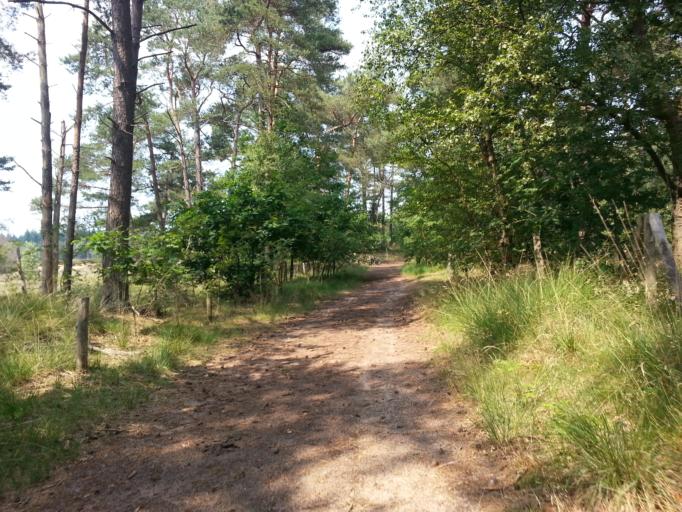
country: NL
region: Utrecht
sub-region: Gemeente Amersfoort
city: Randenbroek
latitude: 52.1231
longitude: 5.3845
